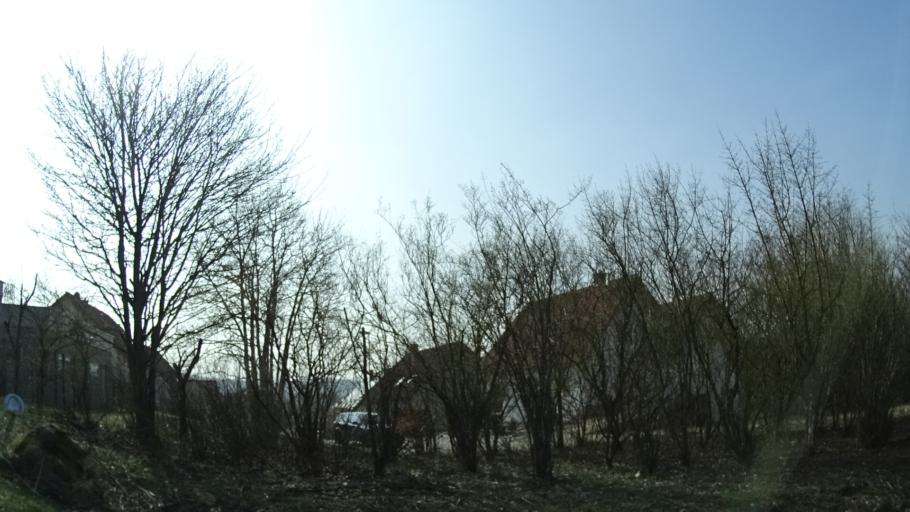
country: DE
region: Rheinland-Pfalz
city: Baumholder
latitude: 49.6114
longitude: 7.3446
